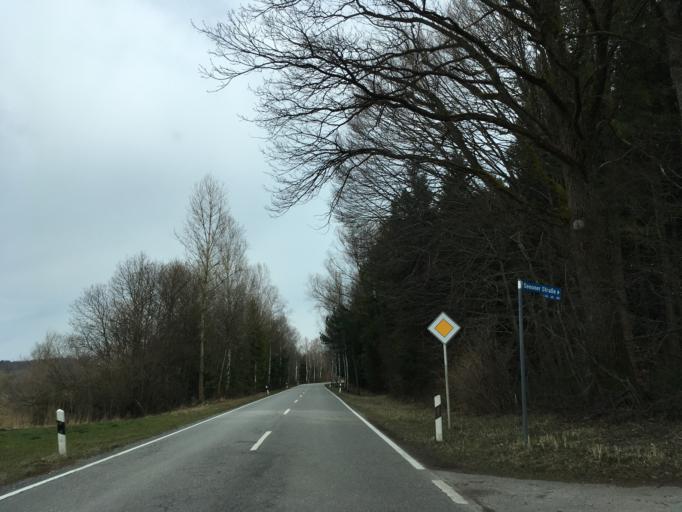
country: DE
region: Bavaria
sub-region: Upper Bavaria
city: Eggstatt
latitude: 47.9395
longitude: 12.3986
